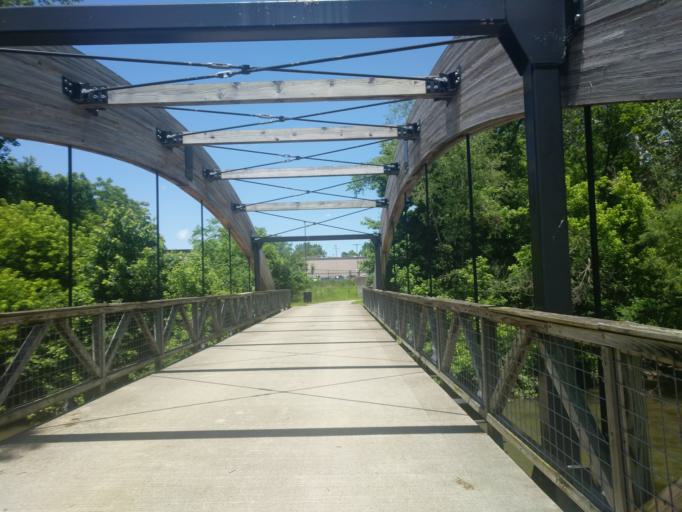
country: US
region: Ohio
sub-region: Franklin County
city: Minerva Park
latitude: 40.0562
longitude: -82.9267
